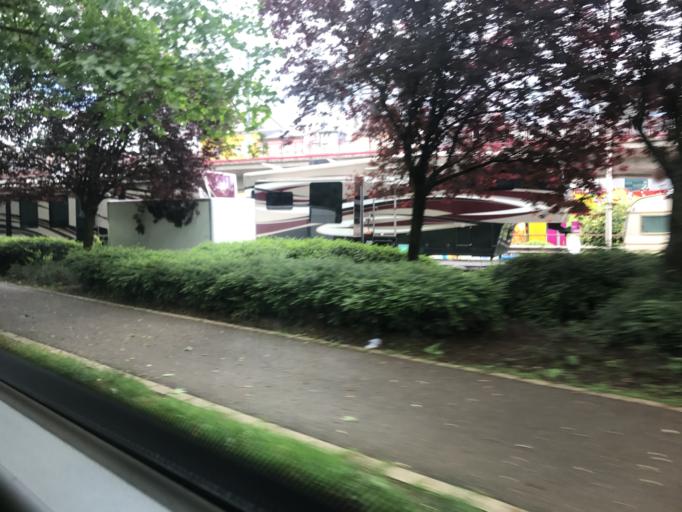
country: LU
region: Luxembourg
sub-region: Canton d'Esch-sur-Alzette
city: Esch-sur-Alzette
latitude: 49.4910
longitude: 5.9750
